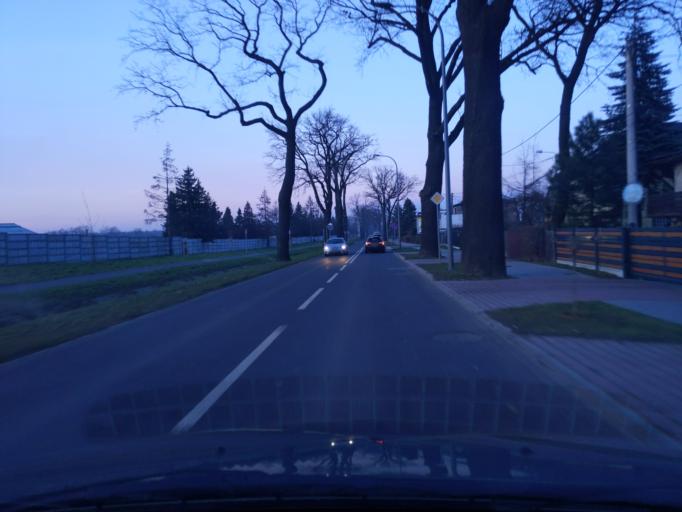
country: PL
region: Silesian Voivodeship
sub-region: Powiat pszczynski
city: Pszczyna
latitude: 49.9641
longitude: 18.9322
